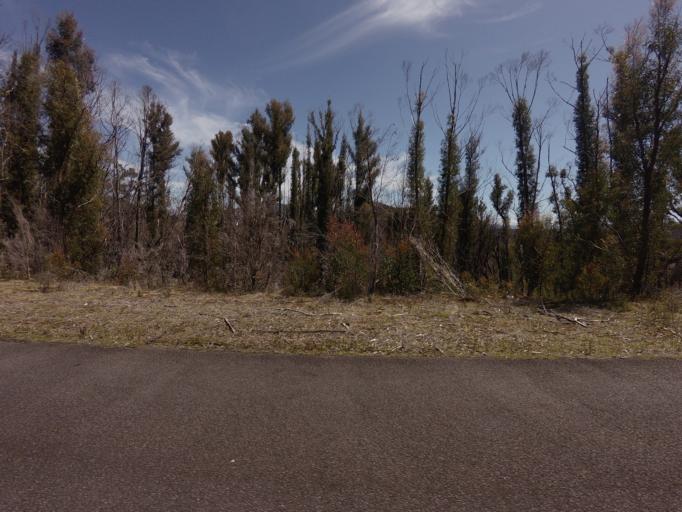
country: AU
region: Tasmania
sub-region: Huon Valley
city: Geeveston
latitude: -42.8481
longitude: 146.2384
